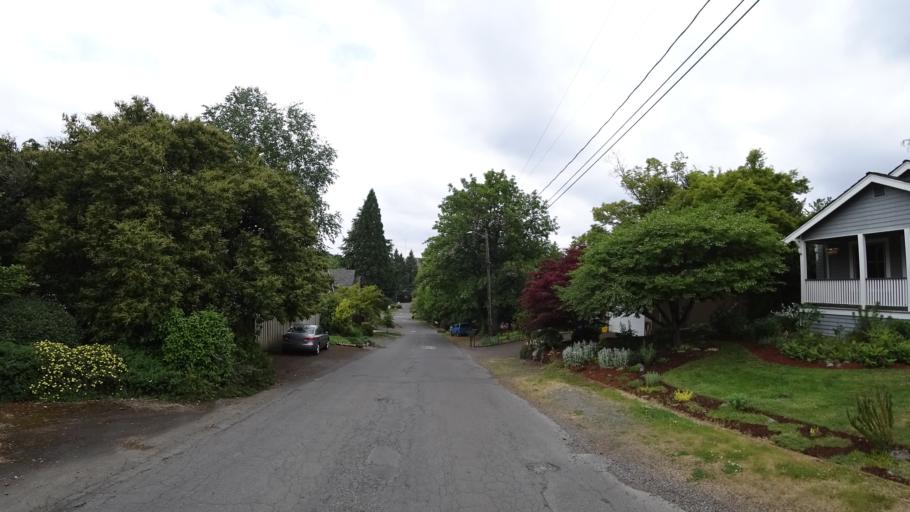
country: US
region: Oregon
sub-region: Washington County
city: Garden Home-Whitford
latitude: 45.4744
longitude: -122.7306
